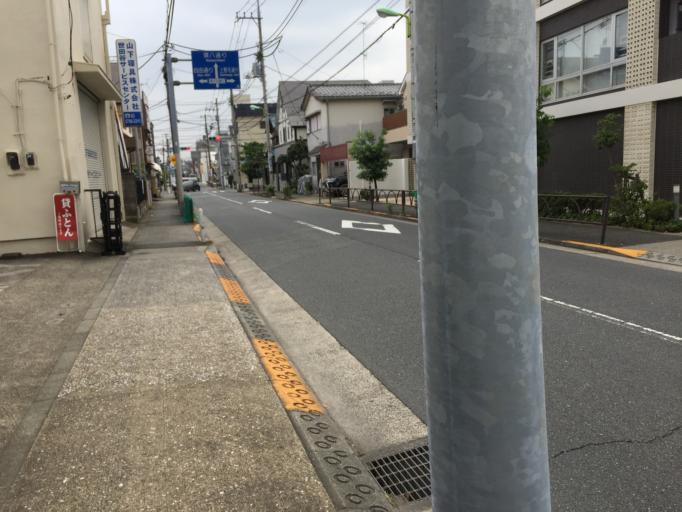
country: JP
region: Tokyo
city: Tokyo
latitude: 35.6073
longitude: 139.6582
